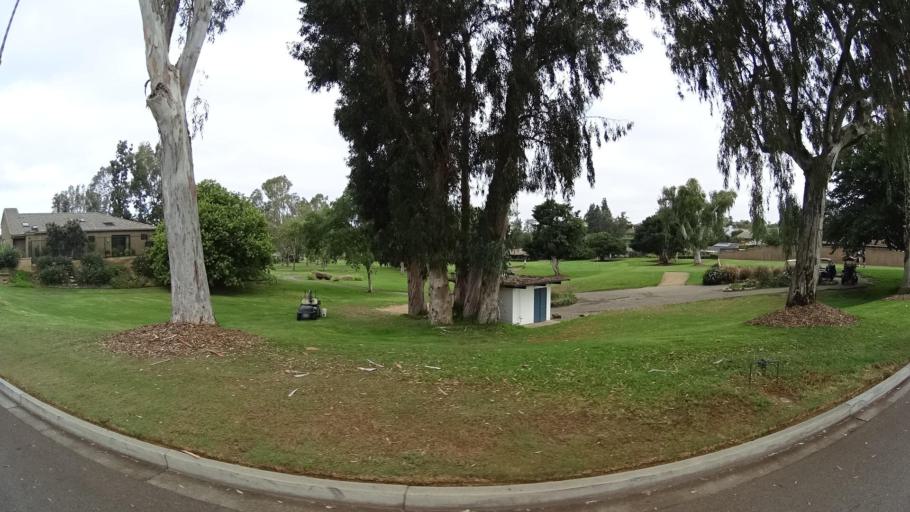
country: US
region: California
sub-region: San Diego County
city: Lake San Marcos
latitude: 33.1186
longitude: -117.1969
